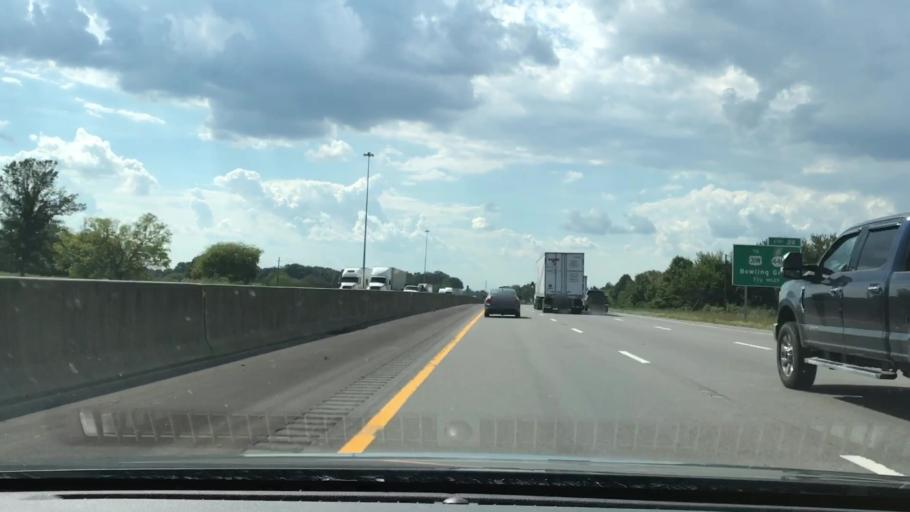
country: US
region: Kentucky
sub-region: Warren County
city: Bowling Green
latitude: 37.0107
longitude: -86.3400
